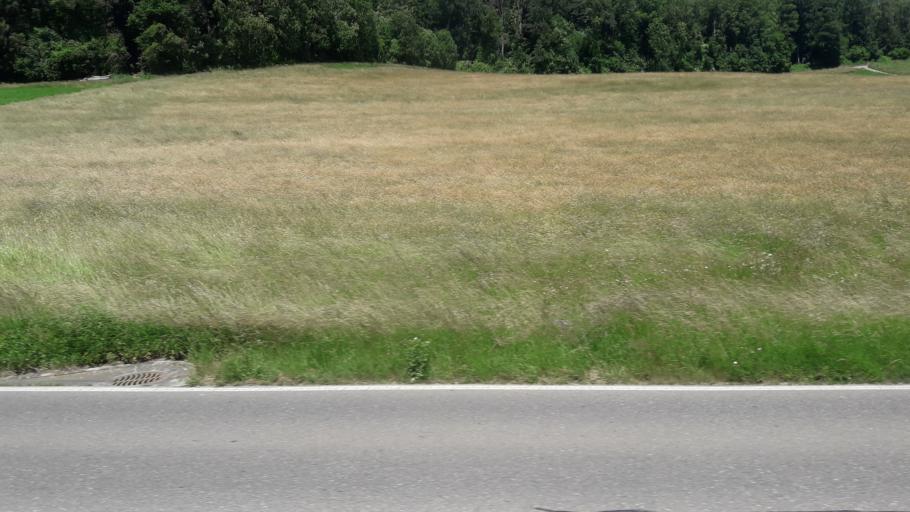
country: CH
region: Bern
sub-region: Seeland District
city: Ins
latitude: 47.0127
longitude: 7.1369
